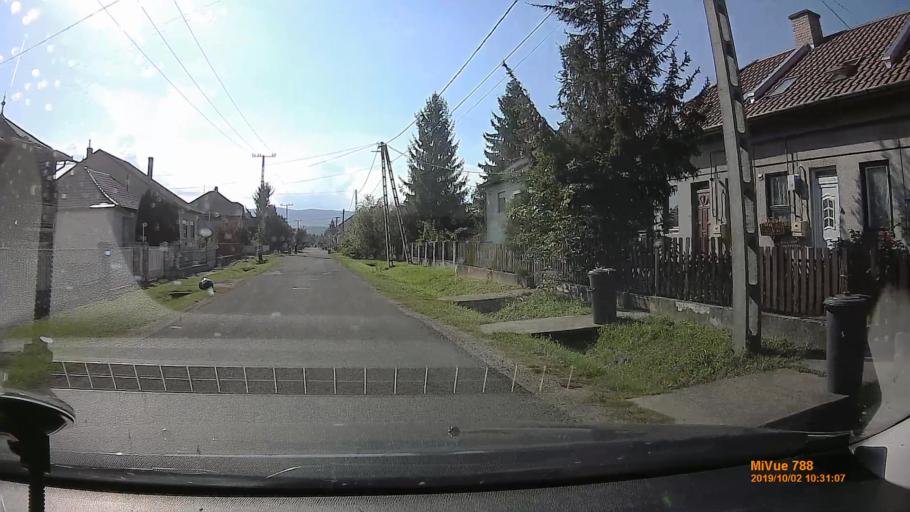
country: HU
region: Nograd
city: Batonyterenye
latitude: 48.0154
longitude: 19.8262
